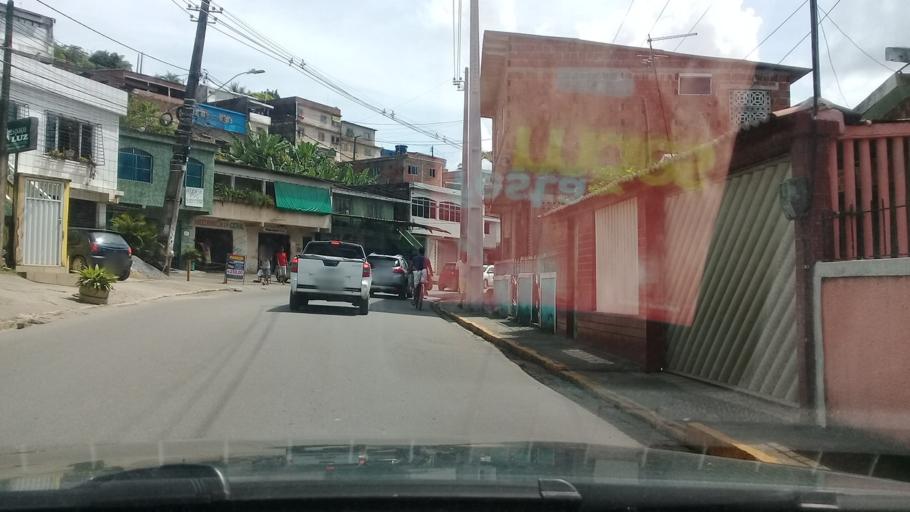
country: BR
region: Pernambuco
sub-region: Jaboatao Dos Guararapes
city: Jaboatao dos Guararapes
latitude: -8.1014
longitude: -35.0195
